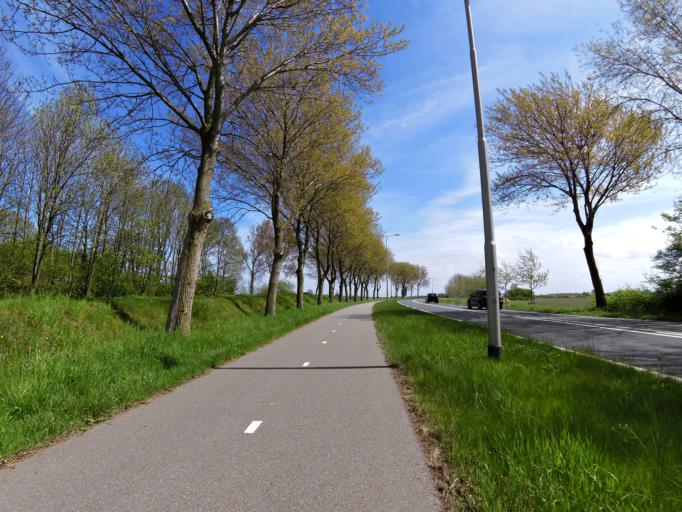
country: NL
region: South Holland
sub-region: Gemeente Hellevoetsluis
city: Nieuw-Helvoet
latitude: 51.8724
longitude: 4.0934
